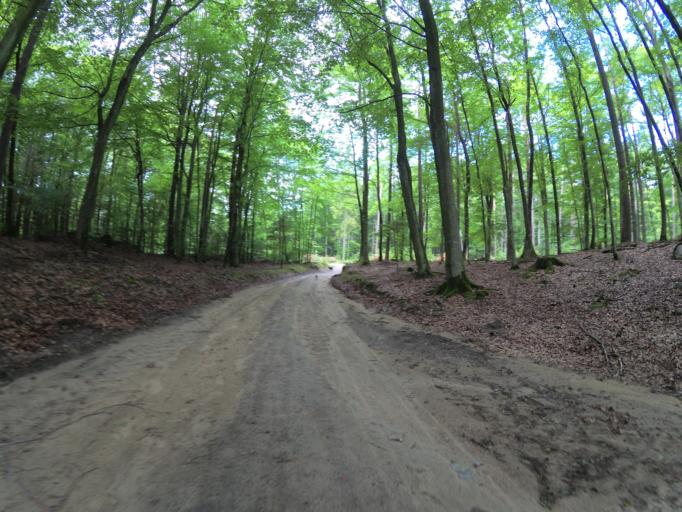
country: PL
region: Pomeranian Voivodeship
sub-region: Powiat wejherowski
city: Bojano
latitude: 54.5073
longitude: 18.4180
